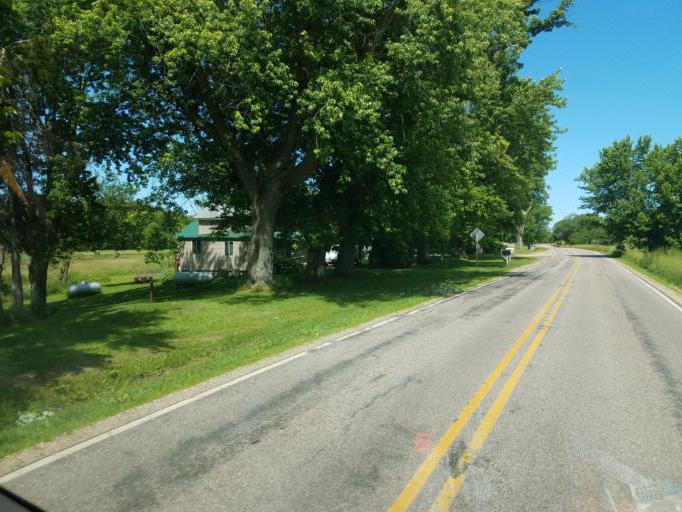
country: US
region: Wisconsin
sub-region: Adams County
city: Adams
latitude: 43.7973
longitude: -89.8743
